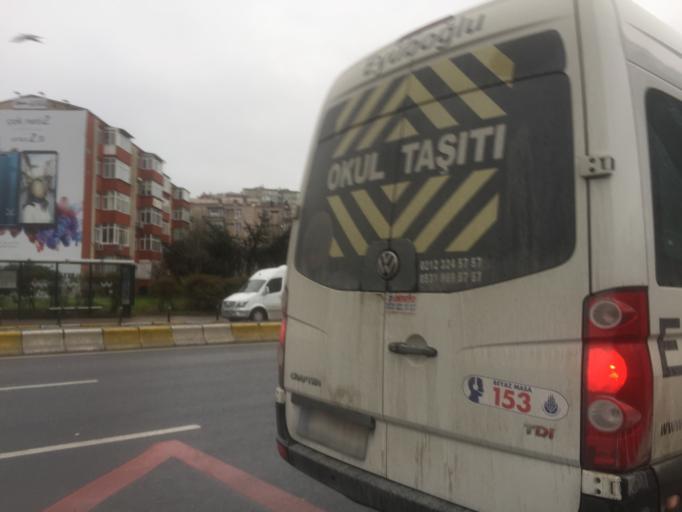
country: TR
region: Istanbul
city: Sisli
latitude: 41.0684
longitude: 29.0085
